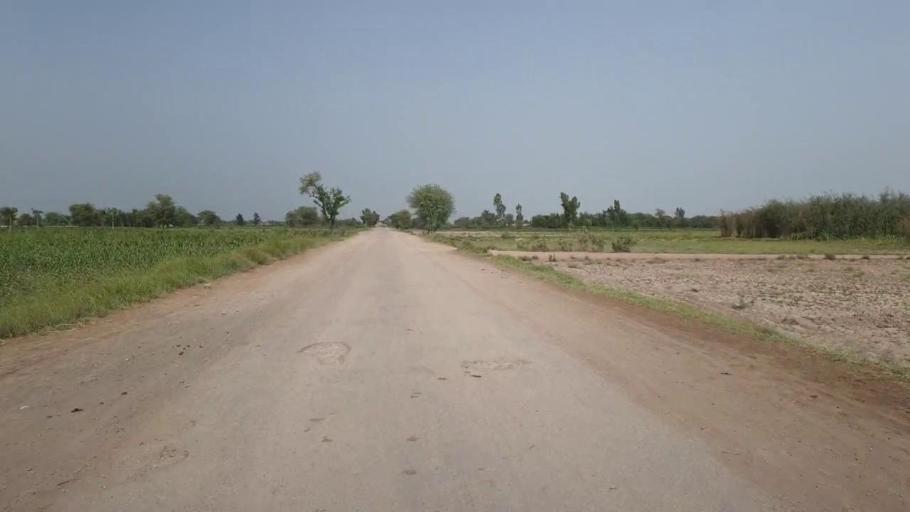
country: PK
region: Sindh
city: Daulatpur
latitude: 26.5485
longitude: 68.0037
